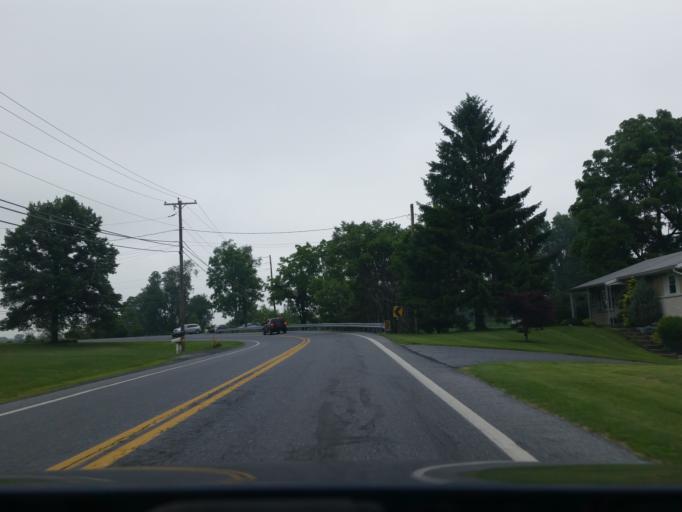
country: US
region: Pennsylvania
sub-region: Lebanon County
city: Jonestown
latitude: 40.3970
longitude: -76.5220
